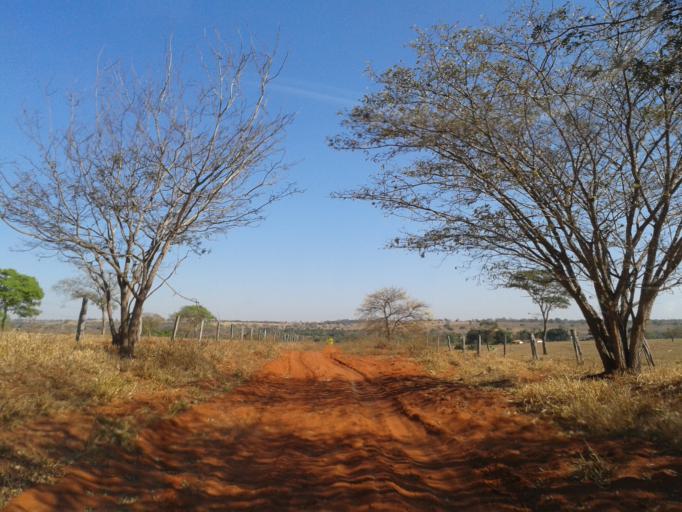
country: BR
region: Minas Gerais
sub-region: Santa Vitoria
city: Santa Vitoria
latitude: -19.0416
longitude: -49.9539
